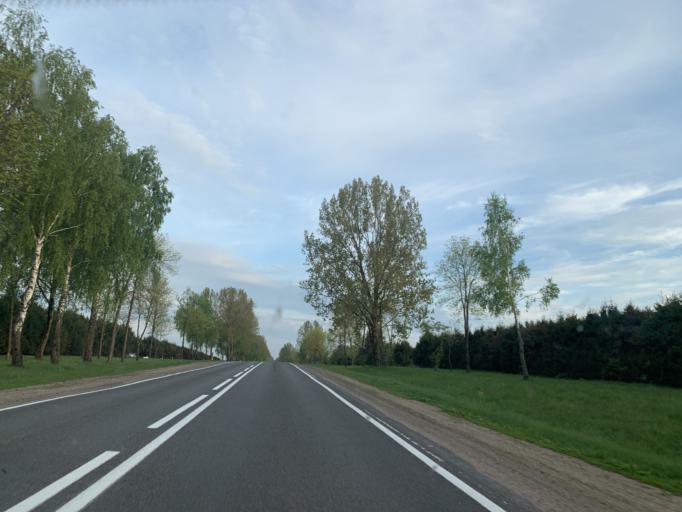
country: BY
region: Minsk
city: Haradzyeya
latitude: 53.3550
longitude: 26.5158
